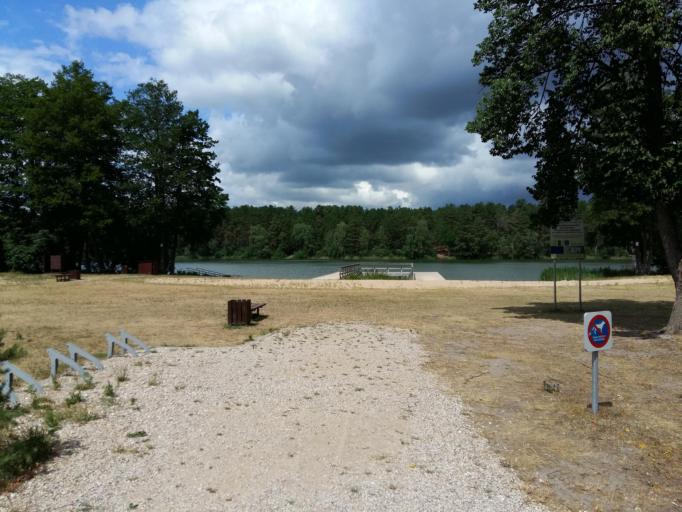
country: LT
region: Alytaus apskritis
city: Druskininkai
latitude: 54.0360
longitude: 24.0804
